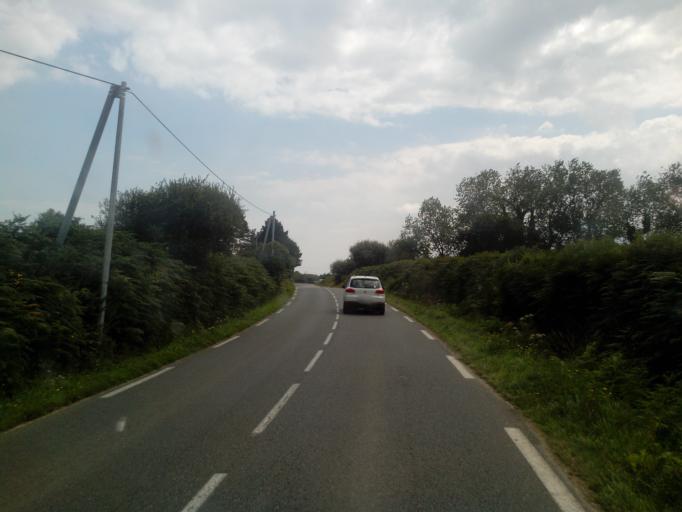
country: FR
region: Brittany
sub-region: Departement des Cotes-d'Armor
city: Plouha
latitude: 48.7073
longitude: -2.9568
